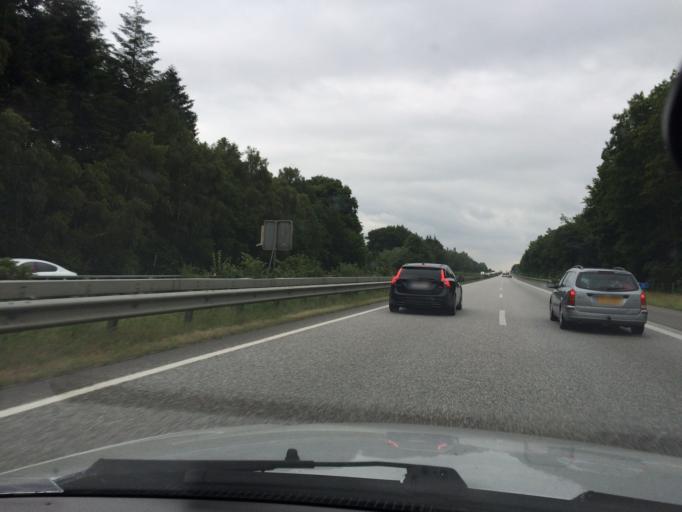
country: DE
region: Schleswig-Holstein
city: Handewitt
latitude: 54.7505
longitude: 9.3742
